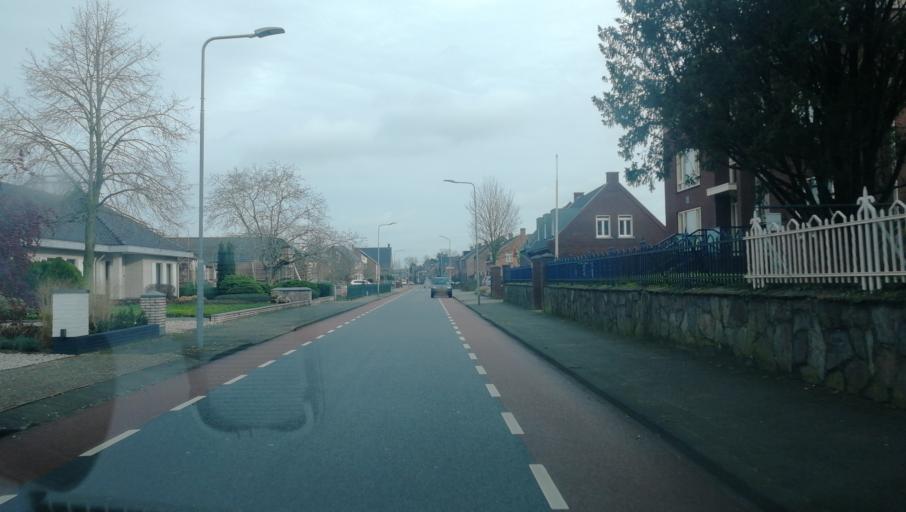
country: NL
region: Limburg
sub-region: Gemeente Venlo
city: Tegelen
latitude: 51.3139
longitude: 6.1162
